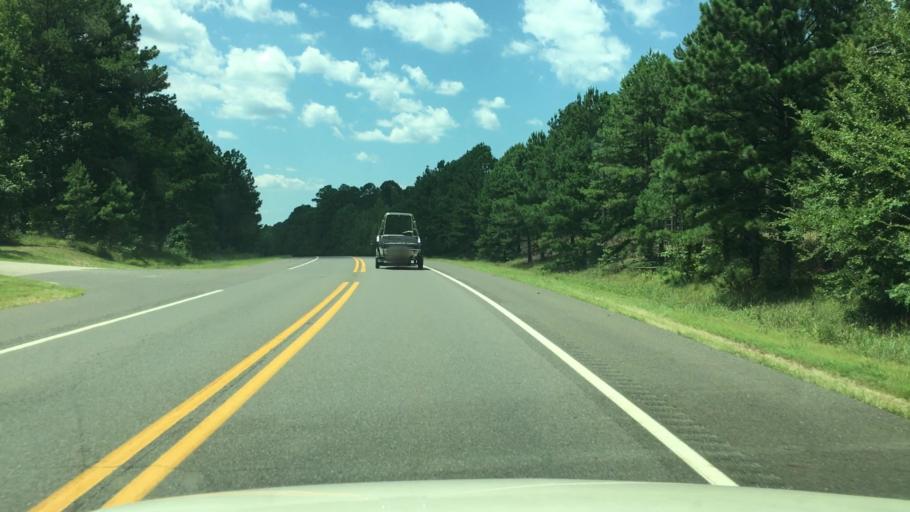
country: US
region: Arkansas
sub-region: Clark County
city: Arkadelphia
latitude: 34.2290
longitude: -93.0918
